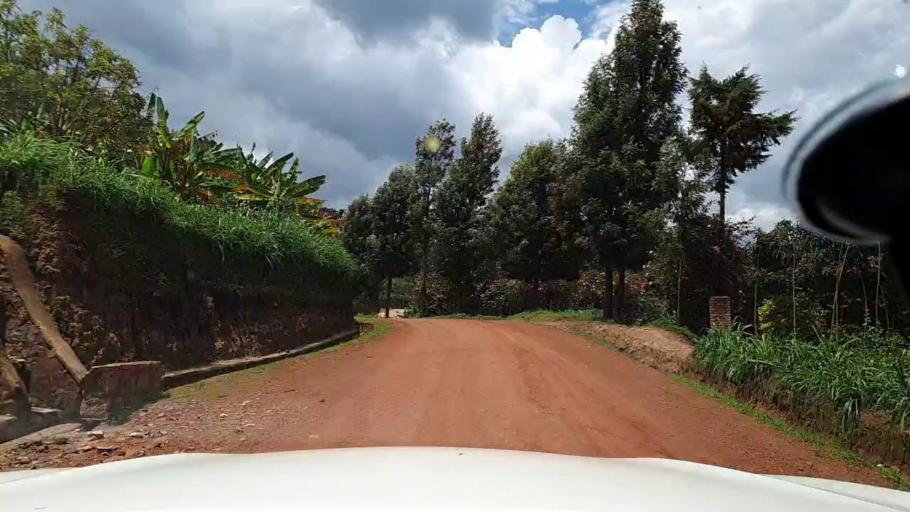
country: RW
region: Northern Province
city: Byumba
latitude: -1.7527
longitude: 29.8461
